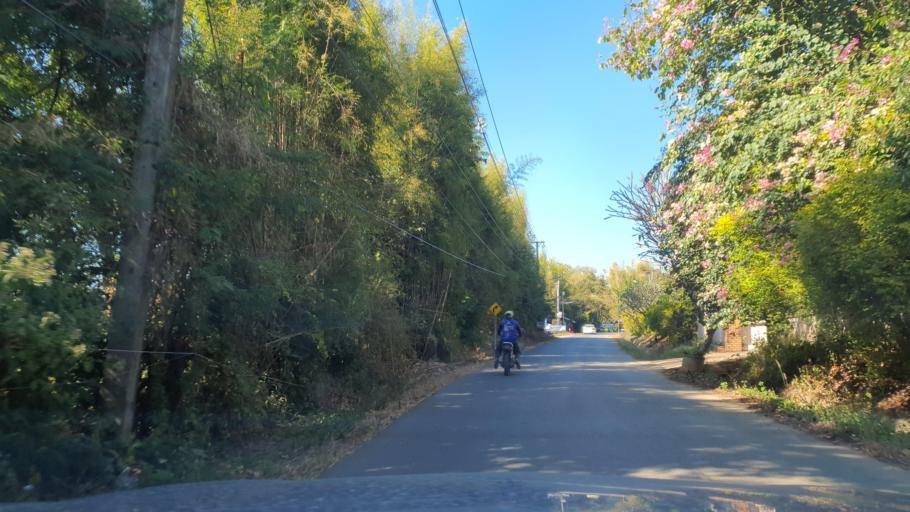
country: TH
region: Chiang Mai
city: Mae Wang
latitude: 18.6831
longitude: 98.8138
